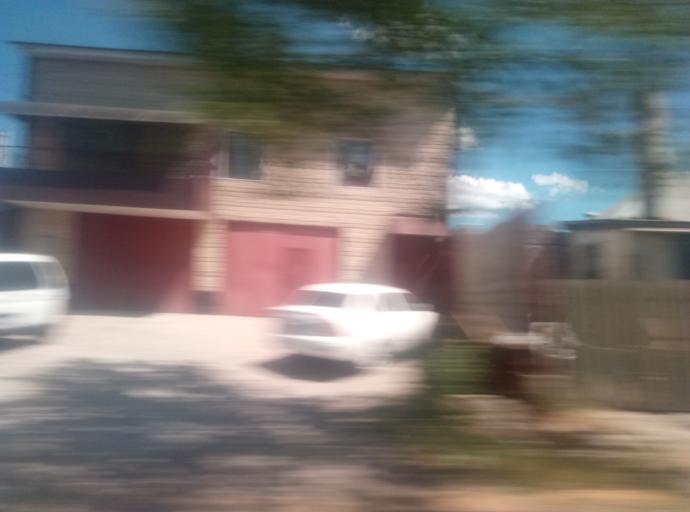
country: RU
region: Tula
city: Kireyevsk
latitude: 53.9705
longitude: 37.9312
